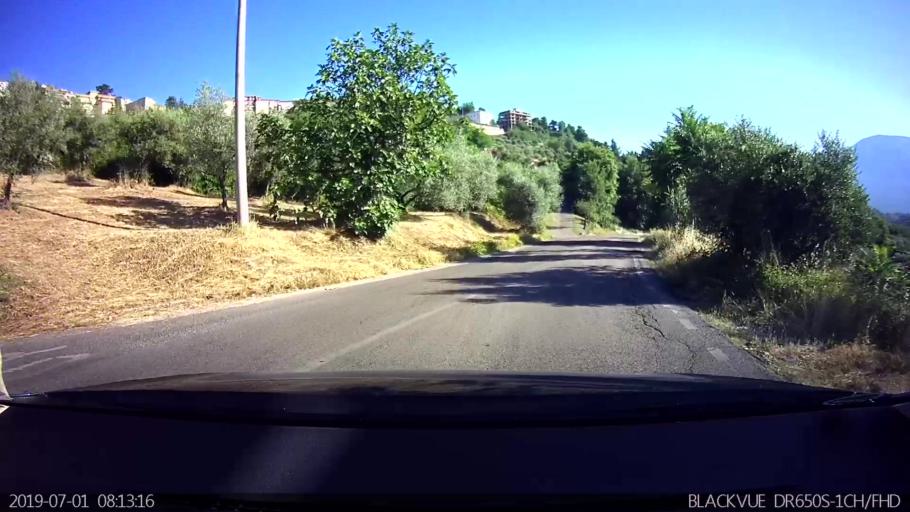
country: IT
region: Latium
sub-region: Provincia di Frosinone
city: Veroli
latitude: 41.6892
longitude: 13.4223
